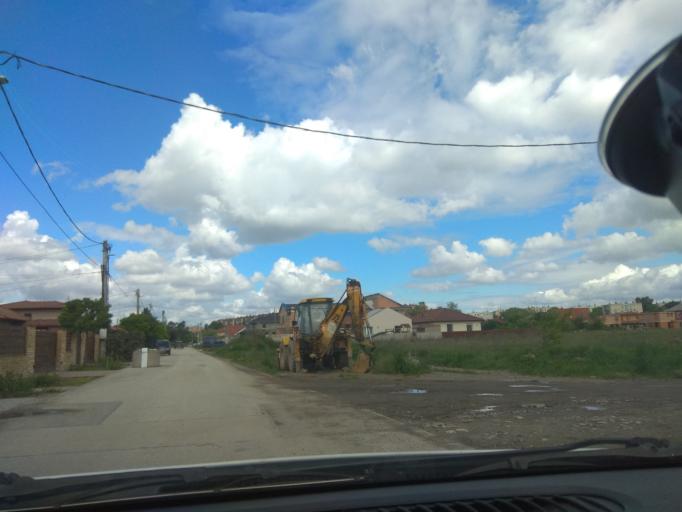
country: HU
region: Budapest
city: Budapest XXI. keruelet
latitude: 47.4020
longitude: 19.0806
